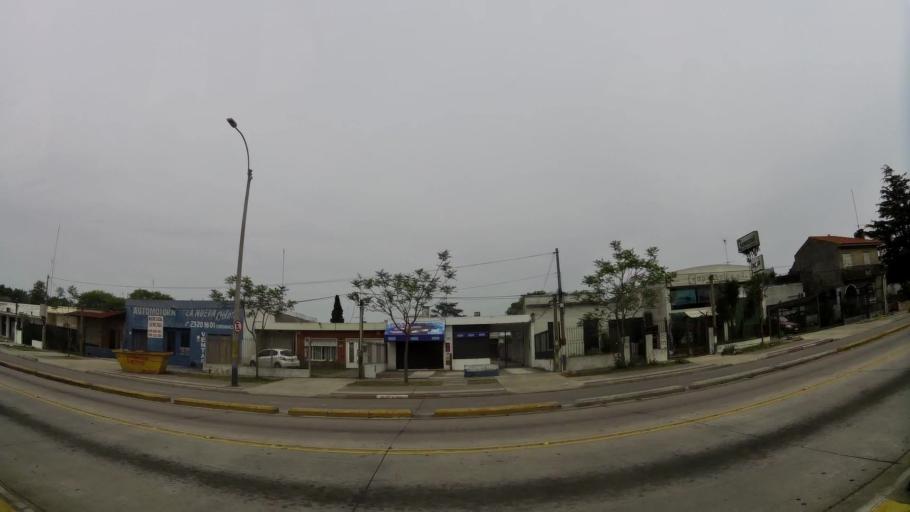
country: UY
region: Canelones
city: La Paz
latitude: -34.8000
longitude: -56.2242
